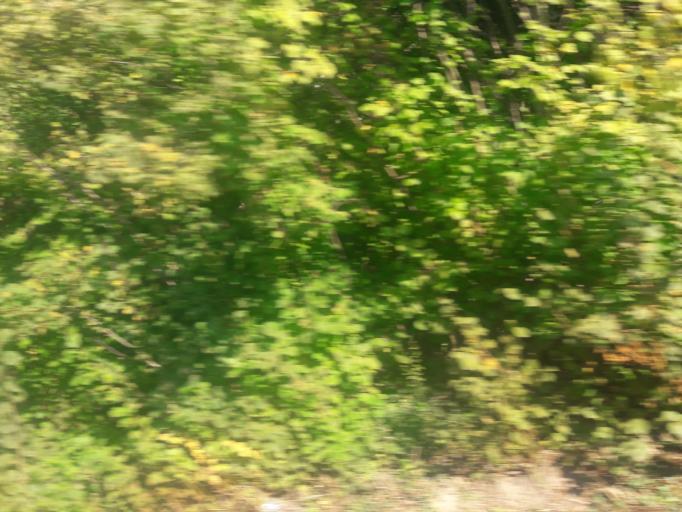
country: CH
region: Lucerne
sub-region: Lucerne-Land District
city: Meggen
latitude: 47.0415
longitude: 8.3523
